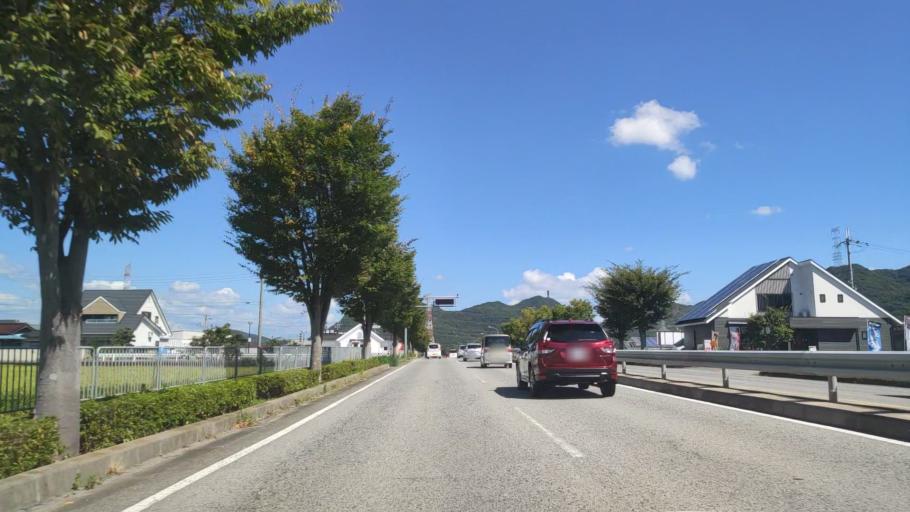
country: JP
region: Hyogo
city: Nishiwaki
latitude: 34.9504
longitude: 134.9708
